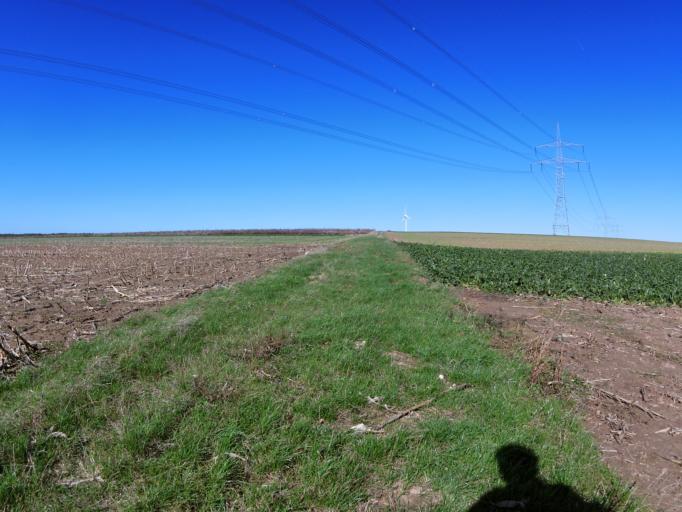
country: DE
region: Bavaria
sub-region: Regierungsbezirk Unterfranken
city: Theilheim
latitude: 49.7360
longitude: 10.0506
